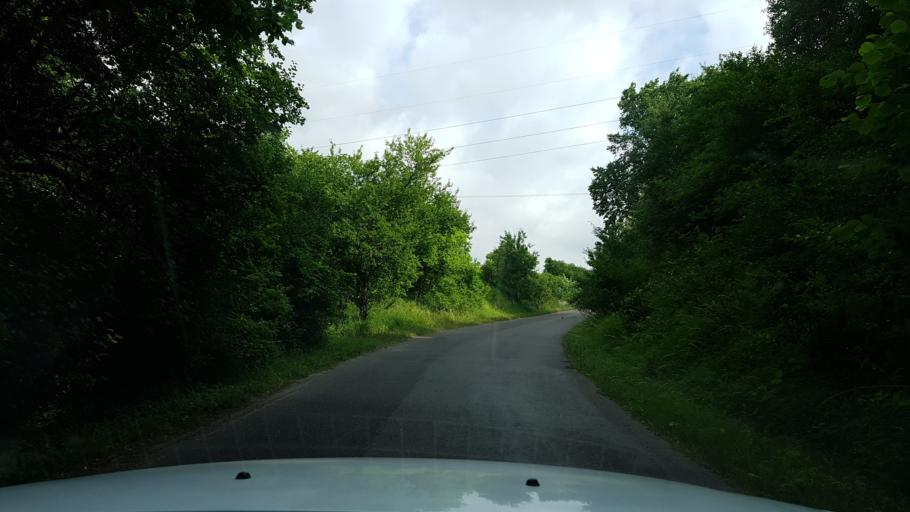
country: PL
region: West Pomeranian Voivodeship
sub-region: Powiat gryfinski
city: Gryfino
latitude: 53.2133
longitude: 14.5944
